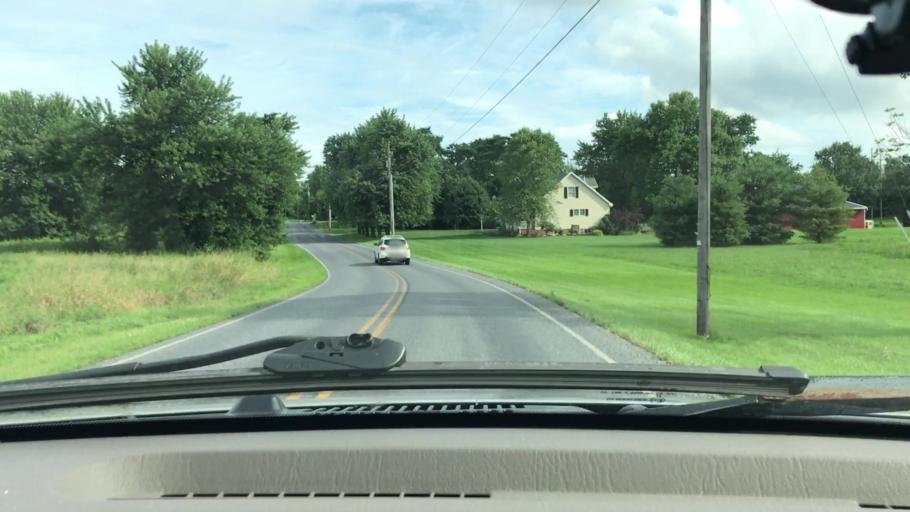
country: US
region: Pennsylvania
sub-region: Lancaster County
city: Elizabethtown
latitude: 40.1672
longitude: -76.5824
